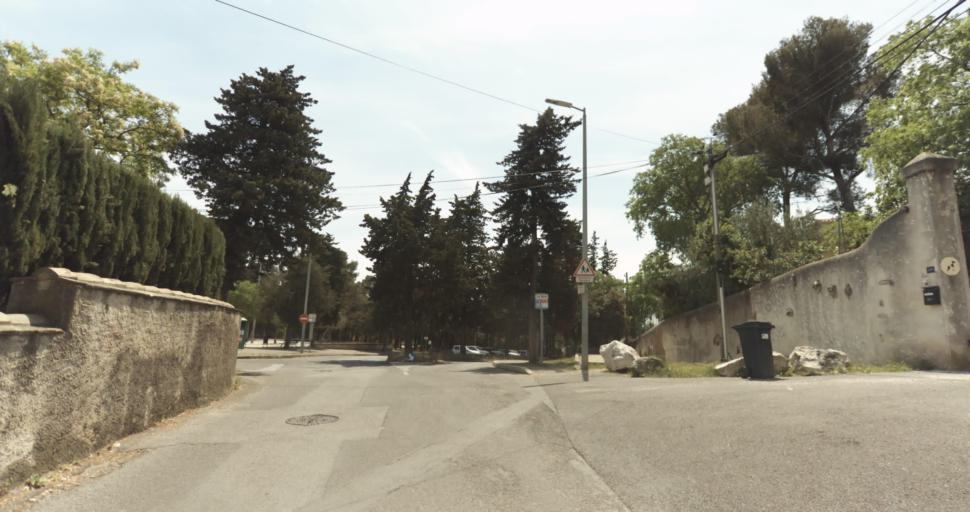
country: FR
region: Languedoc-Roussillon
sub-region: Departement du Gard
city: Nimes
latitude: 43.8457
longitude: 4.3647
